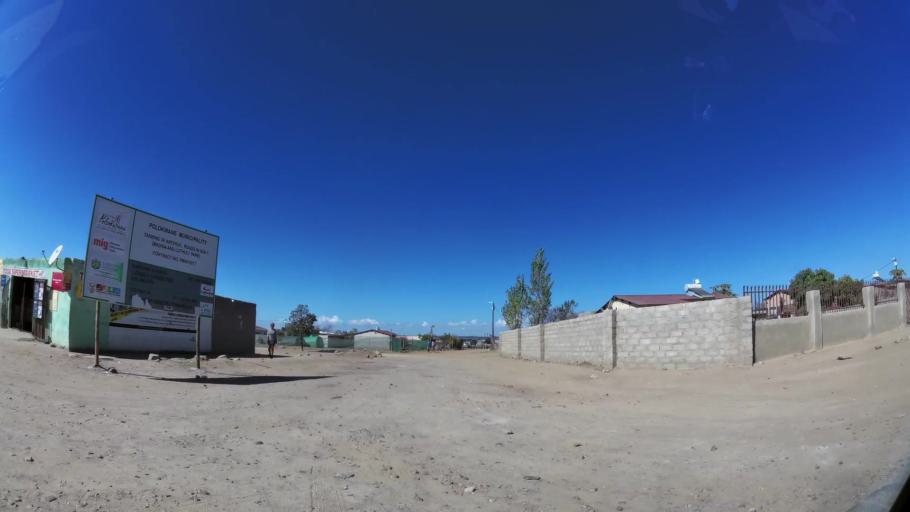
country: ZA
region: Limpopo
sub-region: Capricorn District Municipality
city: Polokwane
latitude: -23.8580
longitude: 29.4124
